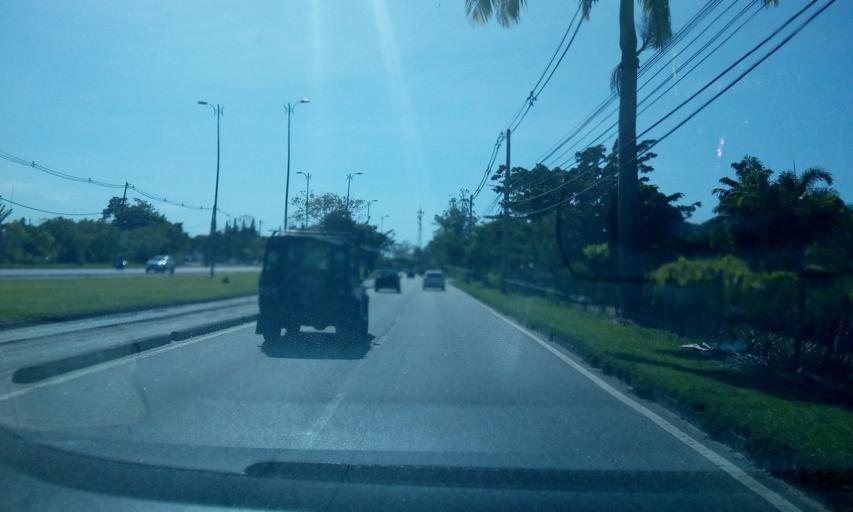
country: BR
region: Rio de Janeiro
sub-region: Nilopolis
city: Nilopolis
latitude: -23.0198
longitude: -43.5040
